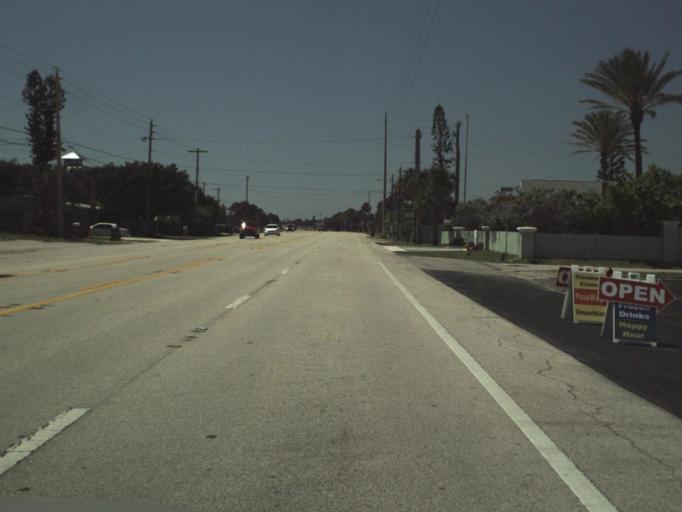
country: US
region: Florida
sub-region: Brevard County
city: Cocoa Beach
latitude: 28.2737
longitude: -80.6070
